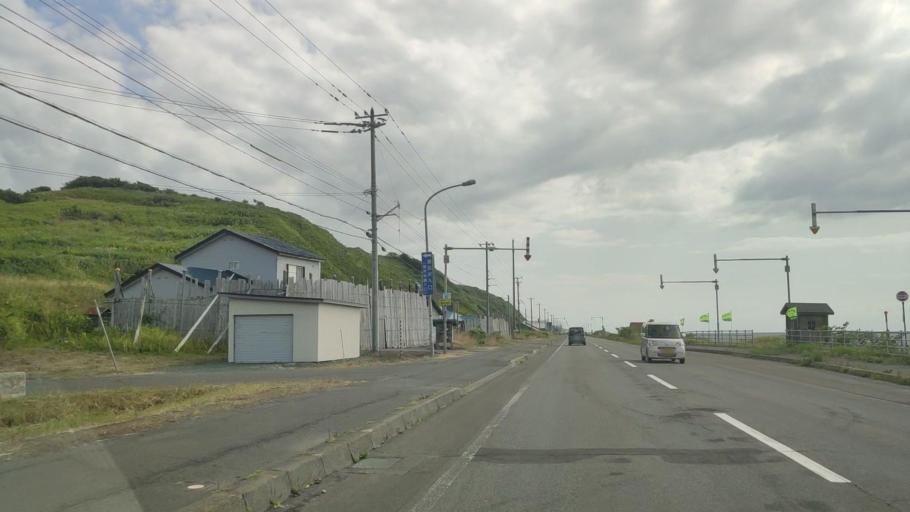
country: JP
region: Hokkaido
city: Rumoi
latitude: 44.2031
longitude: 141.6581
